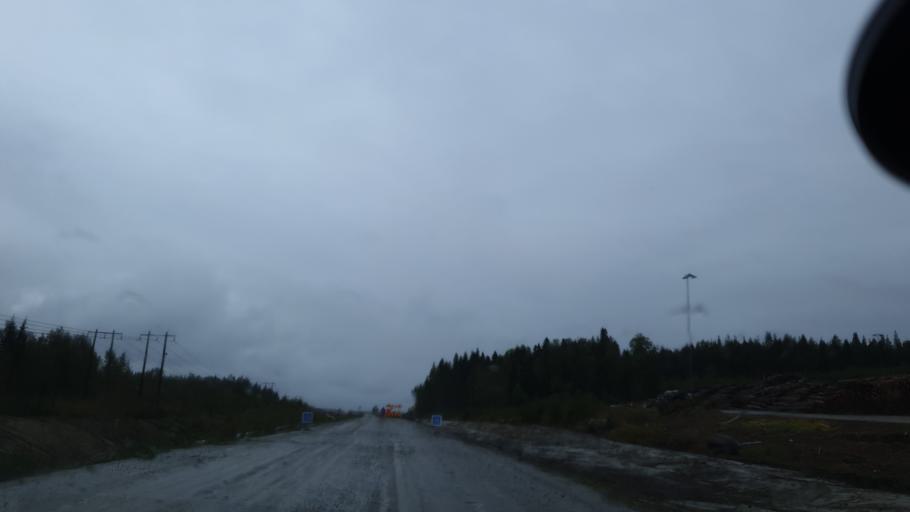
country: SE
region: Vaesterbotten
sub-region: Skelleftea Kommun
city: Soedra Bergsbyn
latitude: 64.7424
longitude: 21.0680
